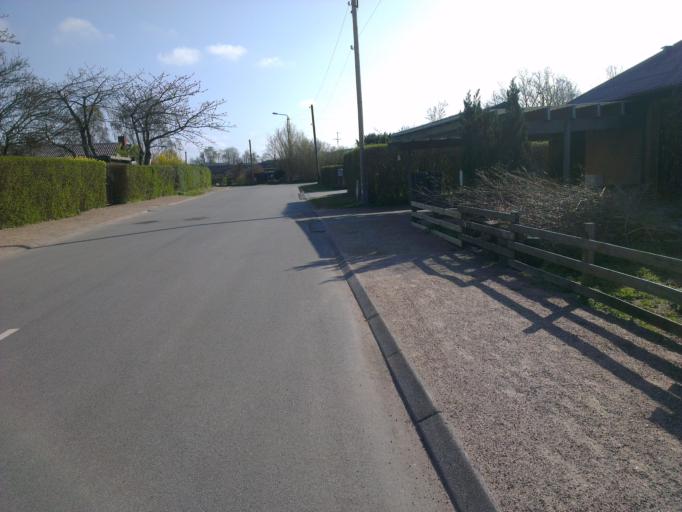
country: DK
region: Capital Region
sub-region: Frederikssund Kommune
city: Frederikssund
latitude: 55.8253
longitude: 12.0758
